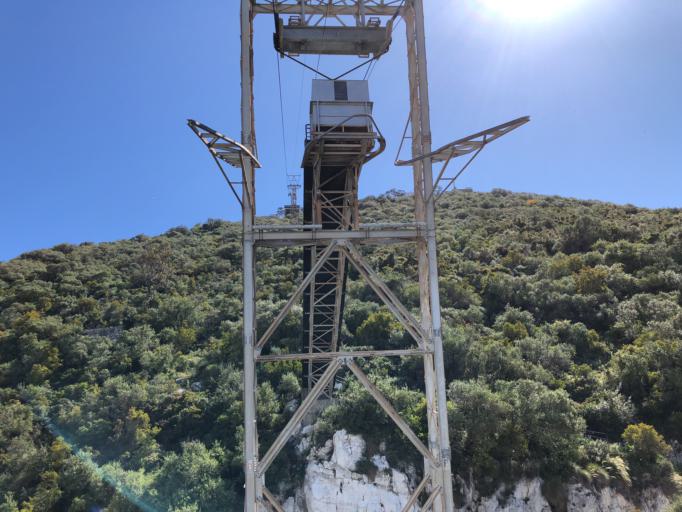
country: GI
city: Gibraltar
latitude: 36.1335
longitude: -5.3493
